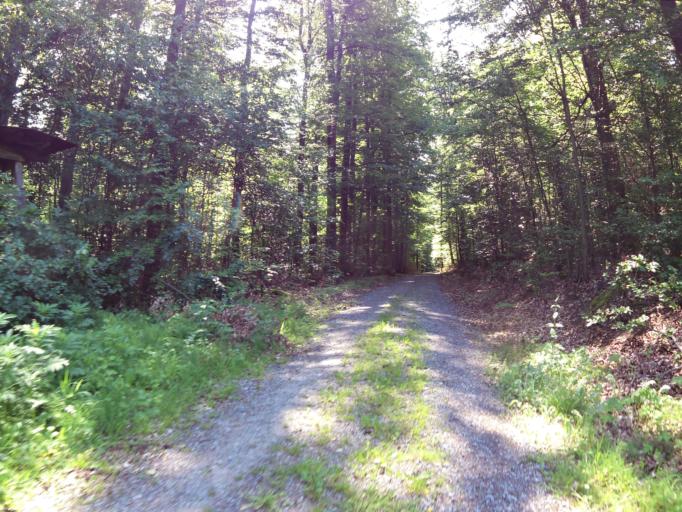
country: DE
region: Bavaria
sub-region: Regierungsbezirk Unterfranken
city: Wuerzburg
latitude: 49.7314
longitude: 9.8830
